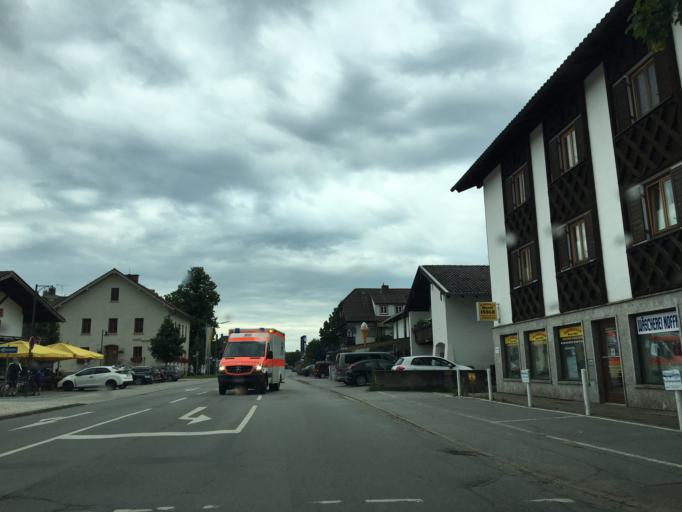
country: DE
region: Bavaria
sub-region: Upper Bavaria
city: Brannenburg
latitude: 47.7348
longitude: 12.1076
